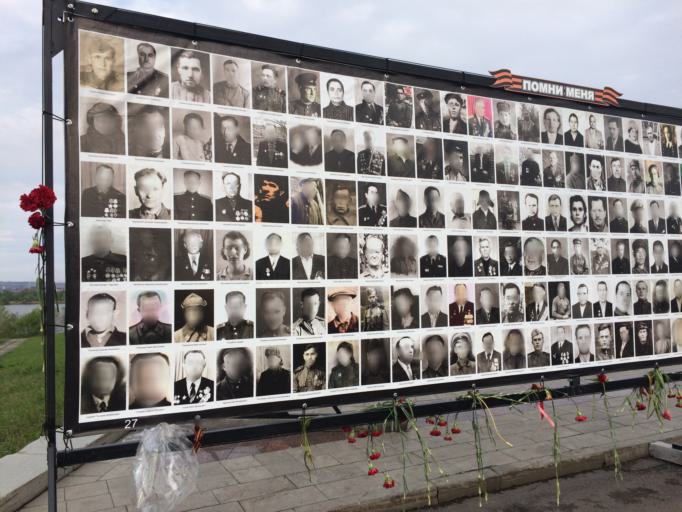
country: RU
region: Chelyabinsk
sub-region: Gorod Magnitogorsk
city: Magnitogorsk
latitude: 53.4078
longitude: 58.9911
